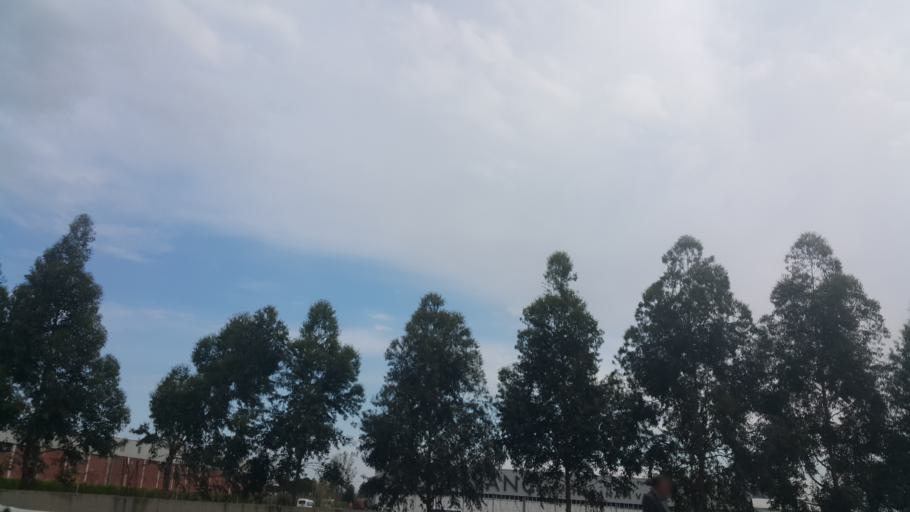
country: TR
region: Mersin
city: Yenice
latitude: 36.9910
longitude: 35.1664
